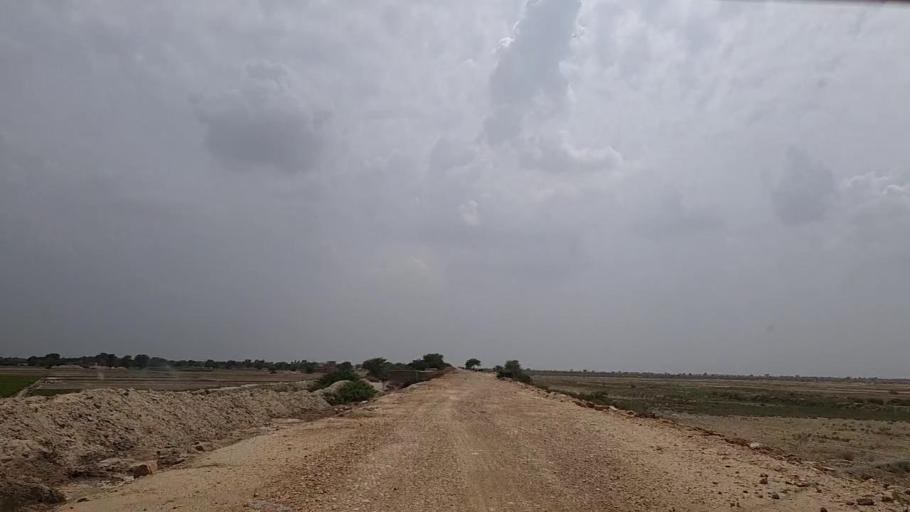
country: PK
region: Sindh
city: Johi
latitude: 26.7395
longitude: 67.5841
